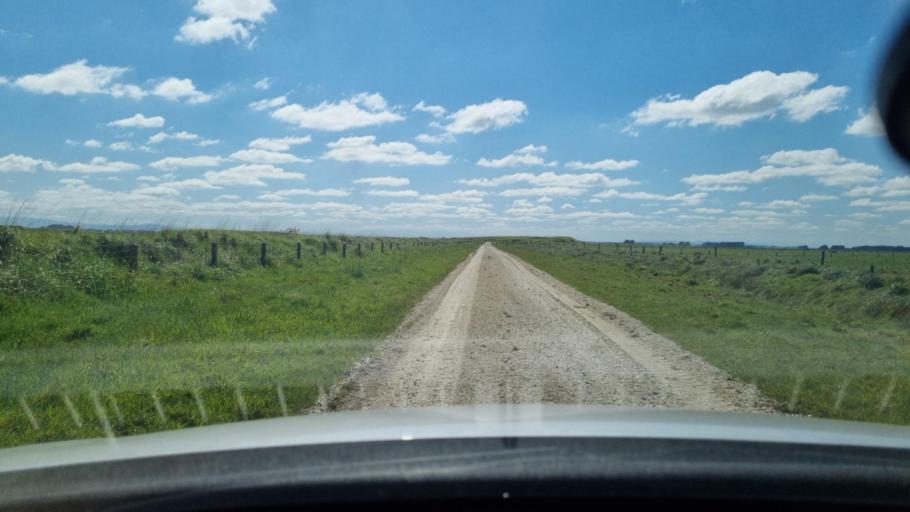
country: NZ
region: Southland
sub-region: Invercargill City
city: Invercargill
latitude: -46.3897
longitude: 168.2594
